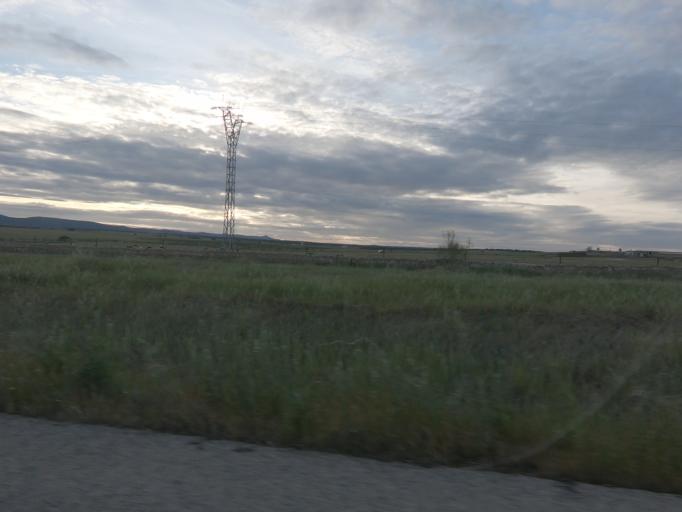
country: ES
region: Extremadura
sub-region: Provincia de Caceres
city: Malpartida de Caceres
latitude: 39.3736
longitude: -6.4533
